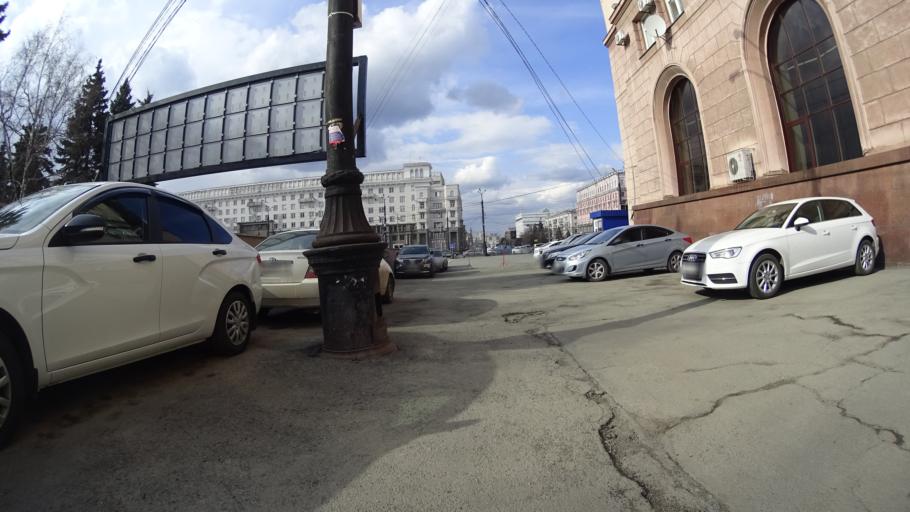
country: RU
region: Chelyabinsk
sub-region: Gorod Chelyabinsk
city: Chelyabinsk
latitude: 55.1596
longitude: 61.4043
